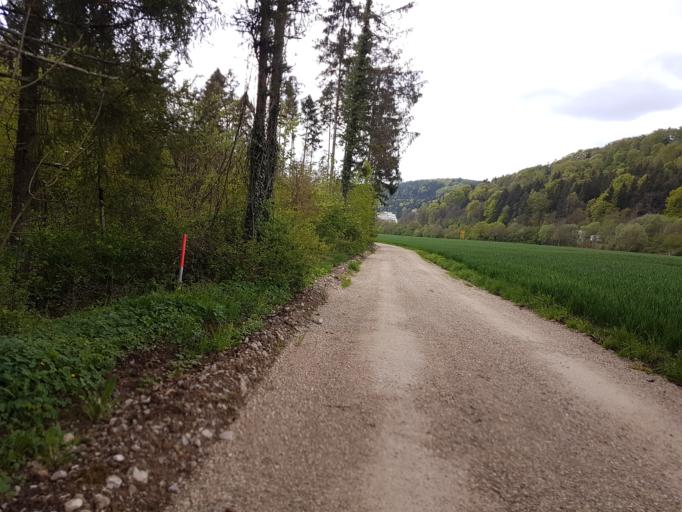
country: CH
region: Schaffhausen
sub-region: Bezirk Schleitheim
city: Schleitheim
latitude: 47.7713
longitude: 8.4835
